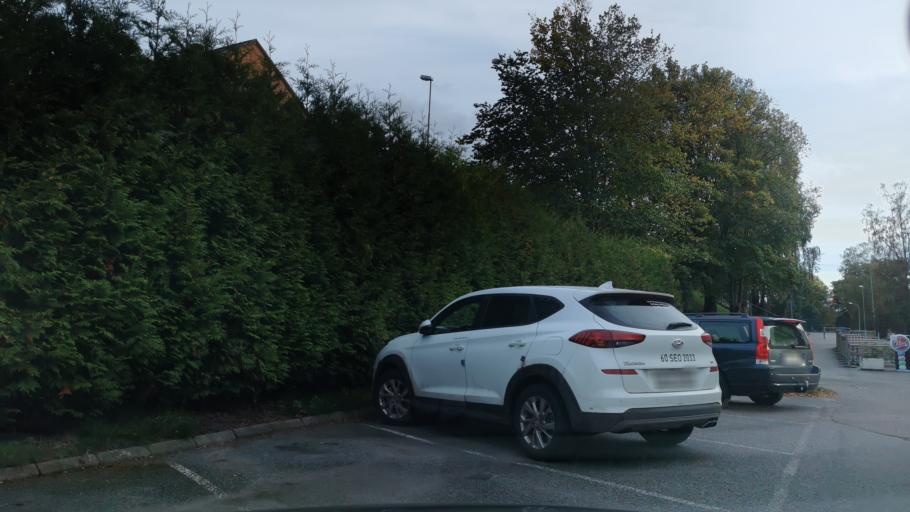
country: SE
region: Vaestra Goetaland
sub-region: Goteborg
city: Eriksbo
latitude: 57.7371
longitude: 12.0298
